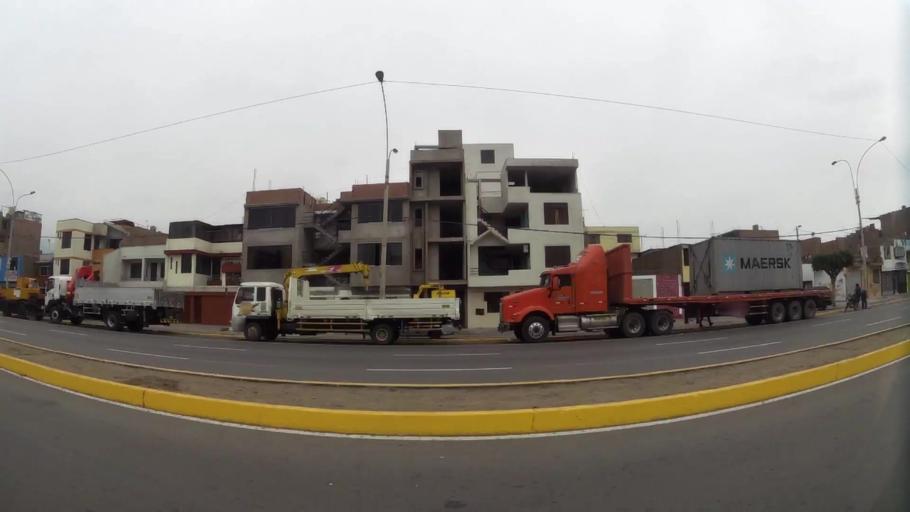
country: PE
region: Lima
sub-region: Lima
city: Independencia
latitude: -11.9783
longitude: -77.0701
